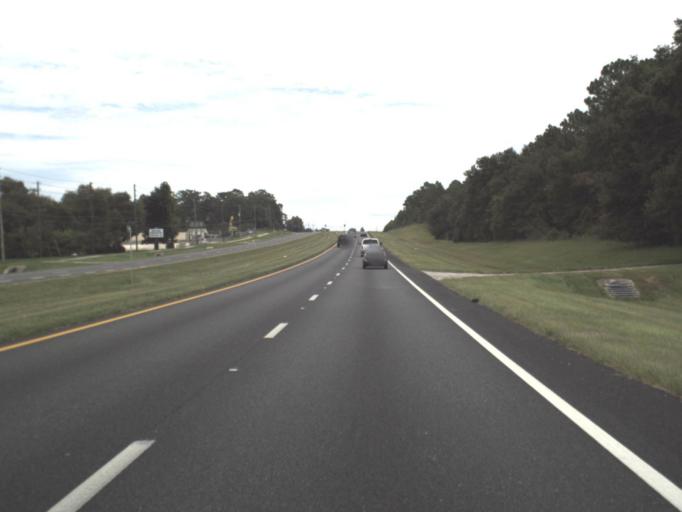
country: US
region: Florida
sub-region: Citrus County
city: Lecanto
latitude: 28.8518
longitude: -82.4760
